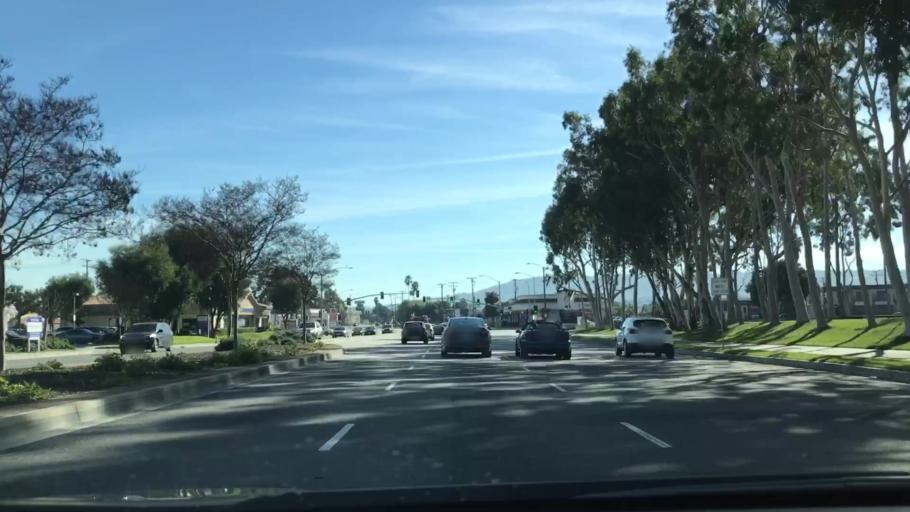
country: US
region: California
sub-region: Los Angeles County
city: Torrance
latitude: 33.8234
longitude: -118.3286
